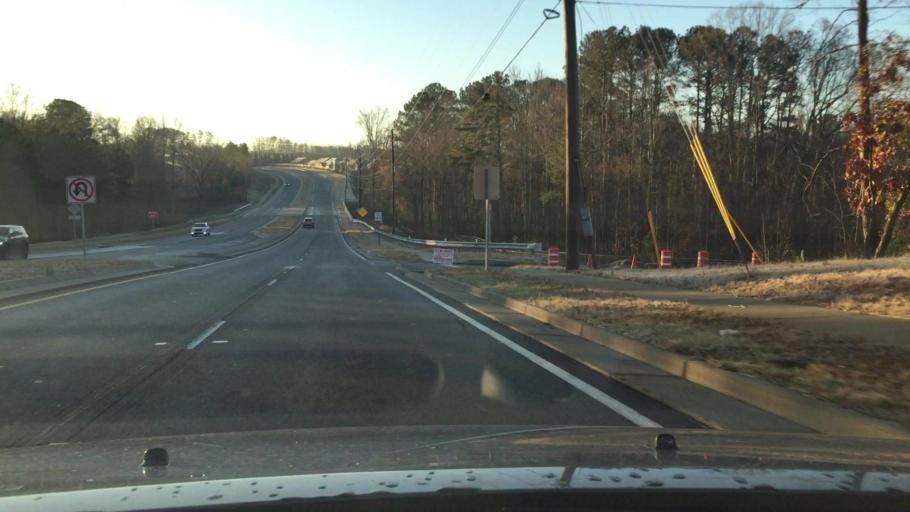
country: US
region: Georgia
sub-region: Forsyth County
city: Cumming
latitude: 34.1820
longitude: -84.1938
